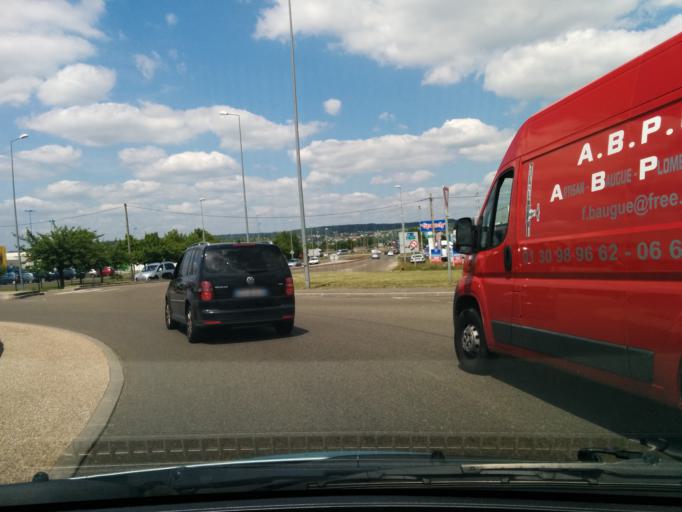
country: FR
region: Ile-de-France
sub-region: Departement des Yvelines
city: Flins-sur-Seine
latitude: 48.9647
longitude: 1.8663
